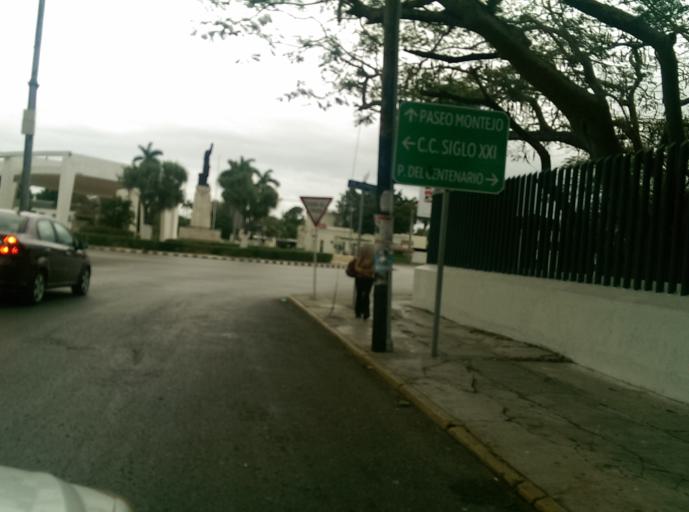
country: MX
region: Yucatan
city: Merida
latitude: 20.9888
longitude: -89.6395
